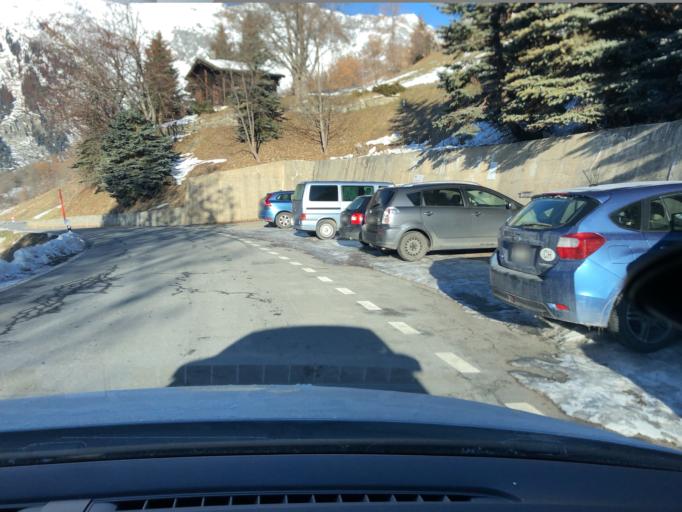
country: CH
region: Valais
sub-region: Goms District
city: Fiesch
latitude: 46.4272
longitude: 8.1538
